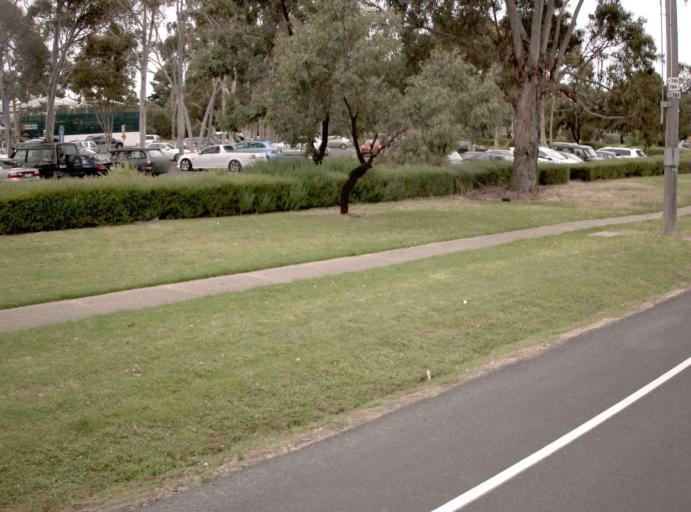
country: AU
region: Victoria
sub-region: Mornington Peninsula
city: Mornington
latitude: -38.2194
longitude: 145.0581
